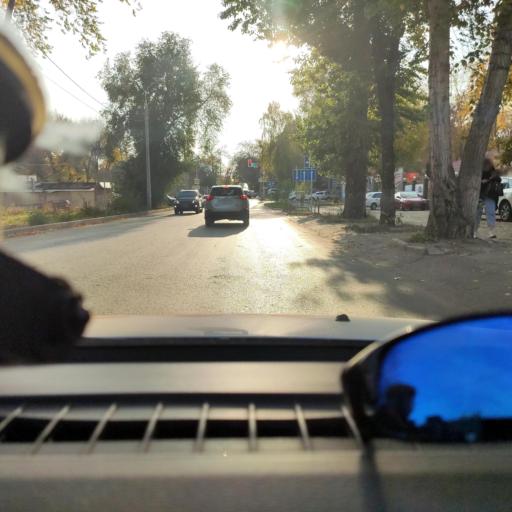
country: RU
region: Samara
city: Samara
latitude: 53.2368
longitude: 50.2431
